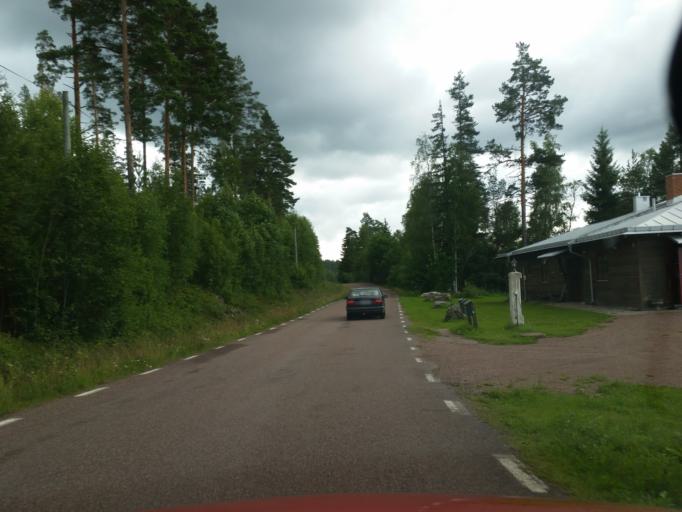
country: SE
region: Dalarna
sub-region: Leksand Municipality
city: Smedby
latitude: 60.6966
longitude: 15.1598
